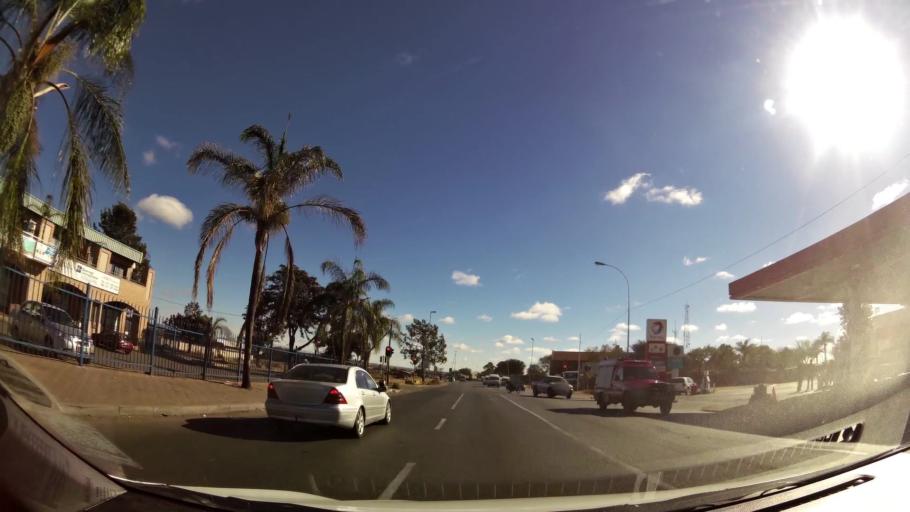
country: ZA
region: Limpopo
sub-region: Capricorn District Municipality
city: Polokwane
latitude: -23.8782
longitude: 29.4416
